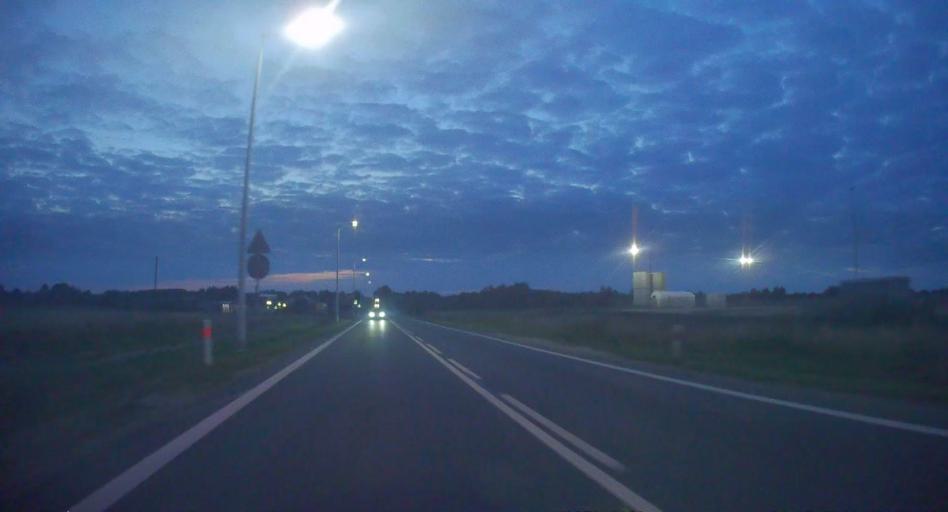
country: PL
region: Silesian Voivodeship
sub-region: Powiat klobucki
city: Kamyk
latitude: 50.8764
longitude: 18.9997
